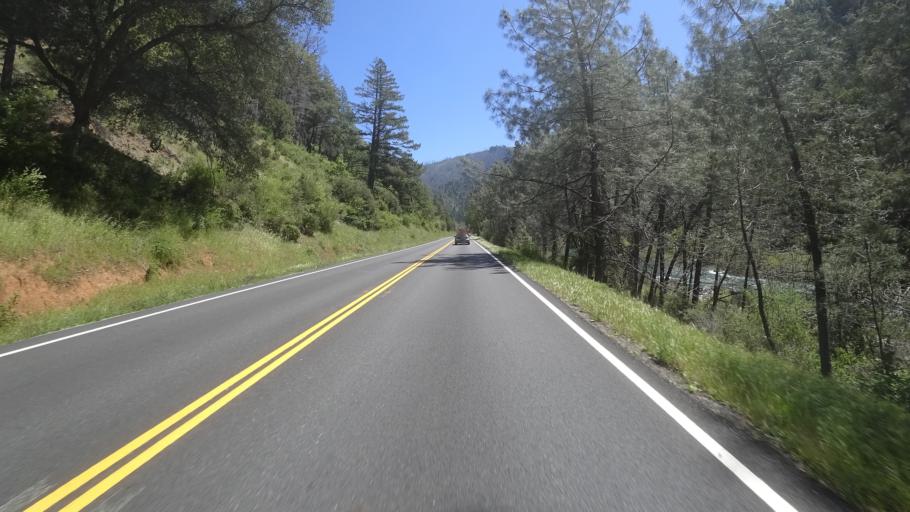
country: US
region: California
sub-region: Humboldt County
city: Willow Creek
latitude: 40.7906
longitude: -123.4346
